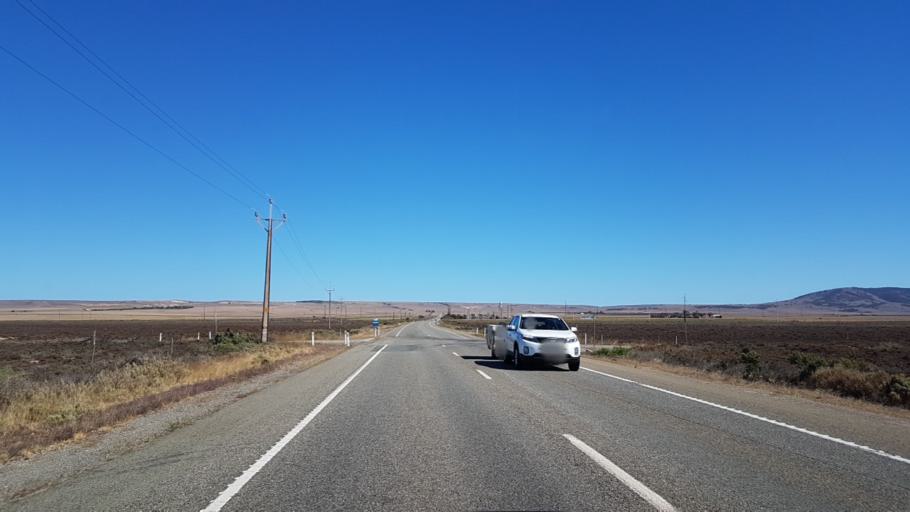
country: AU
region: South Australia
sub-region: Wakefield
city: Balaklava
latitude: -34.0952
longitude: 138.0993
